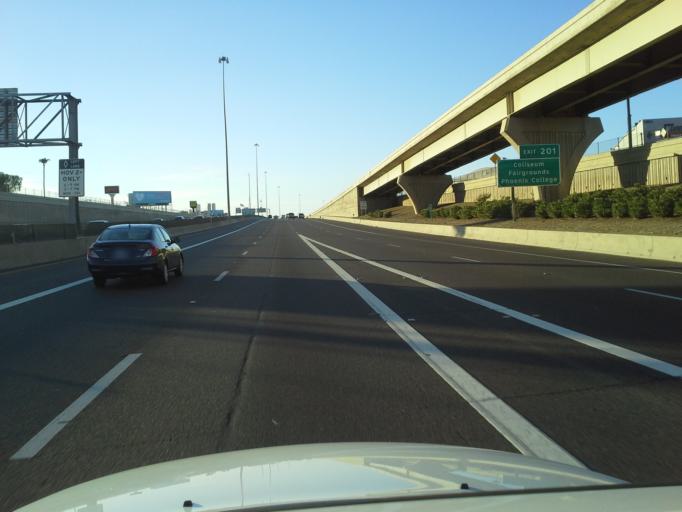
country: US
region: Arizona
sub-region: Maricopa County
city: Phoenix
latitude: 33.4666
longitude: -112.1100
